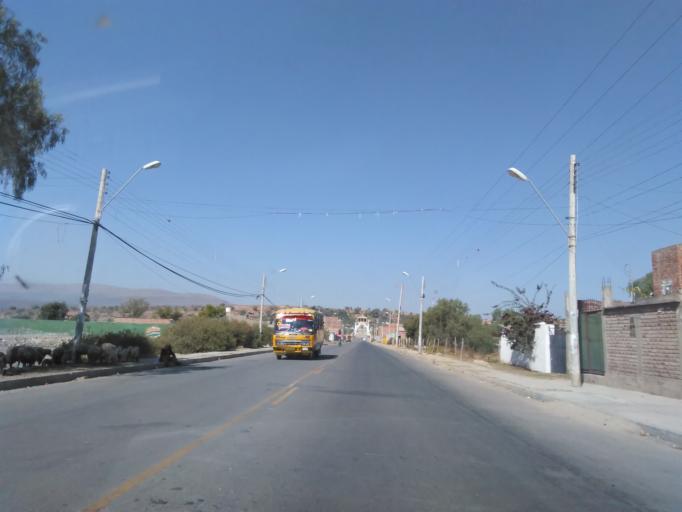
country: BO
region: Cochabamba
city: Sipe Sipe
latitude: -17.4148
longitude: -66.2830
